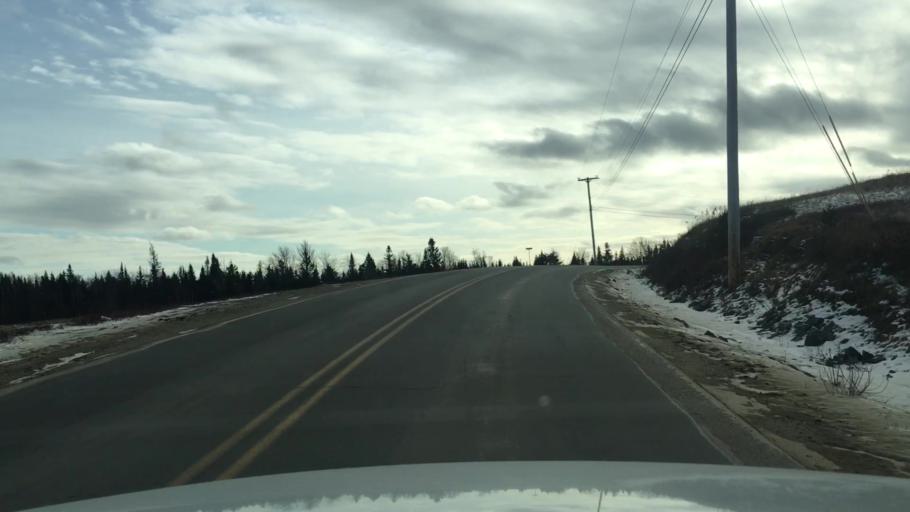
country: US
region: Maine
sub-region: Washington County
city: Jonesport
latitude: 44.6230
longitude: -67.6016
